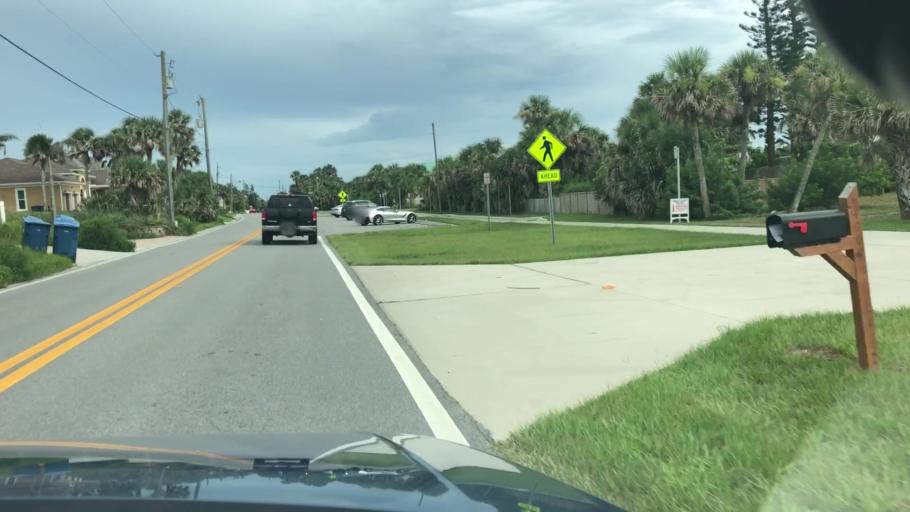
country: US
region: Florida
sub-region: Volusia County
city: Port Orange
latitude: 29.1324
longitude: -80.9584
